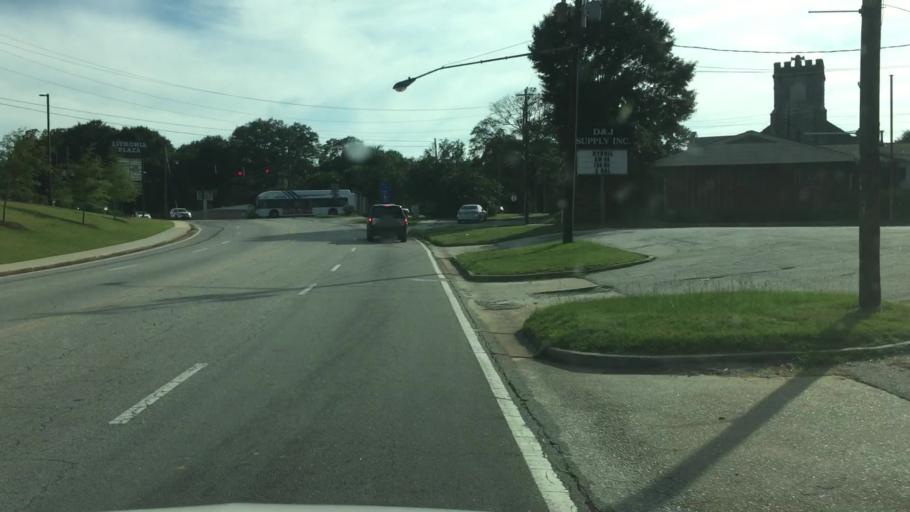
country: US
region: Georgia
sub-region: DeKalb County
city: Lithonia
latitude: 33.7135
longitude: -84.1070
